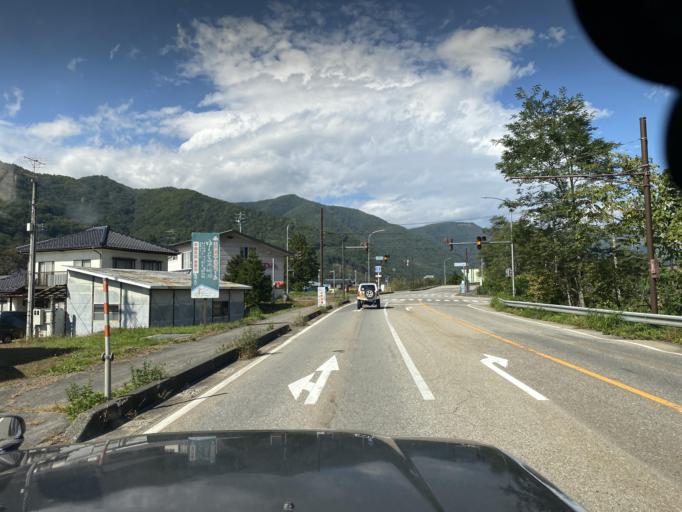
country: JP
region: Nagano
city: Omachi
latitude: 36.5392
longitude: 137.8432
